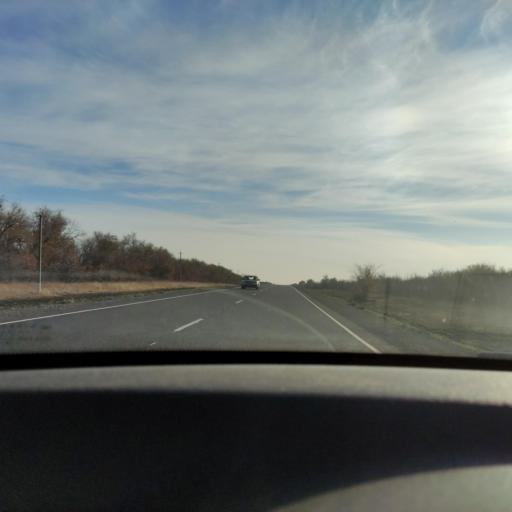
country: RU
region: Samara
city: Krasnoarmeyskoye
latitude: 52.8262
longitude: 50.0080
